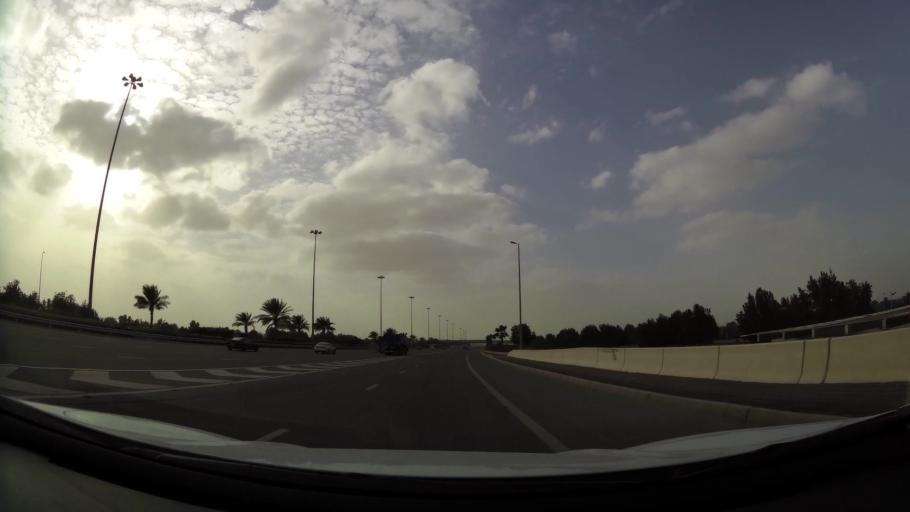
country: AE
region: Abu Dhabi
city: Abu Dhabi
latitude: 24.4902
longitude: 54.6258
